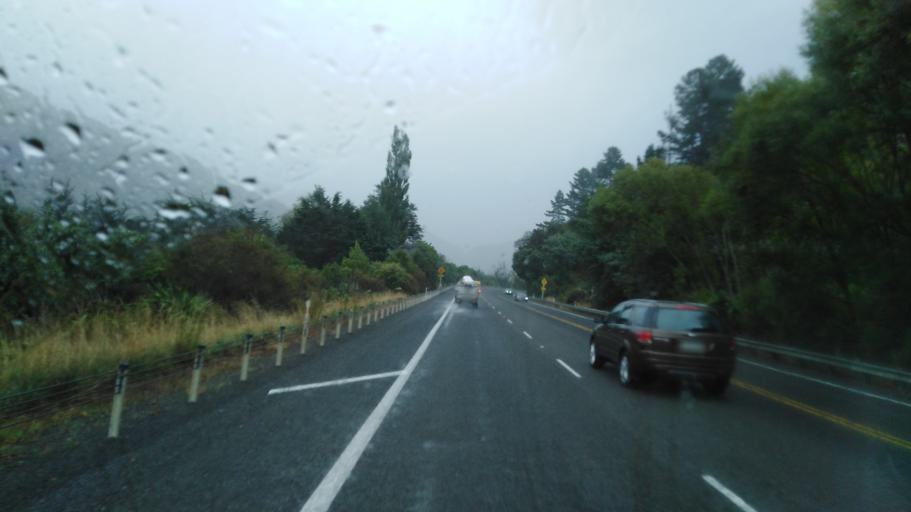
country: NZ
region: Marlborough
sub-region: Marlborough District
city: Picton
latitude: -41.3811
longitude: 173.9482
